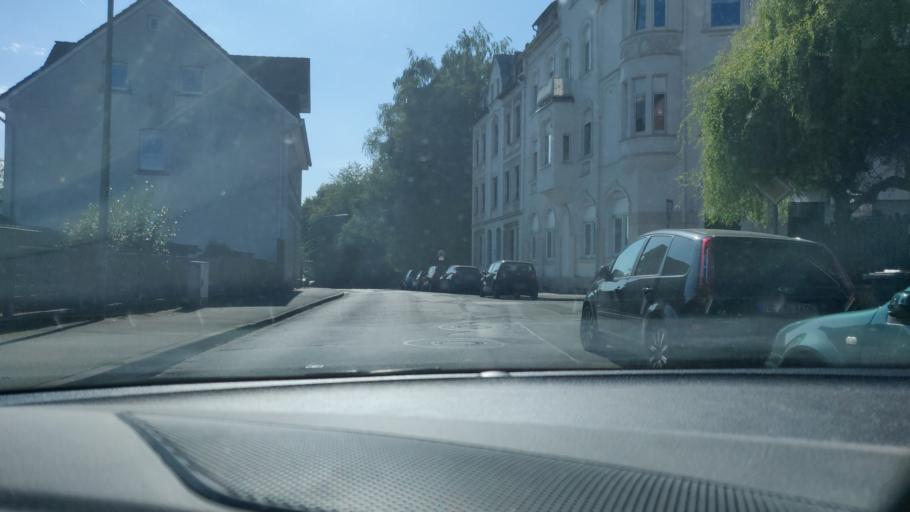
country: DE
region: North Rhine-Westphalia
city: Hattingen
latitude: 51.3622
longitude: 7.1237
